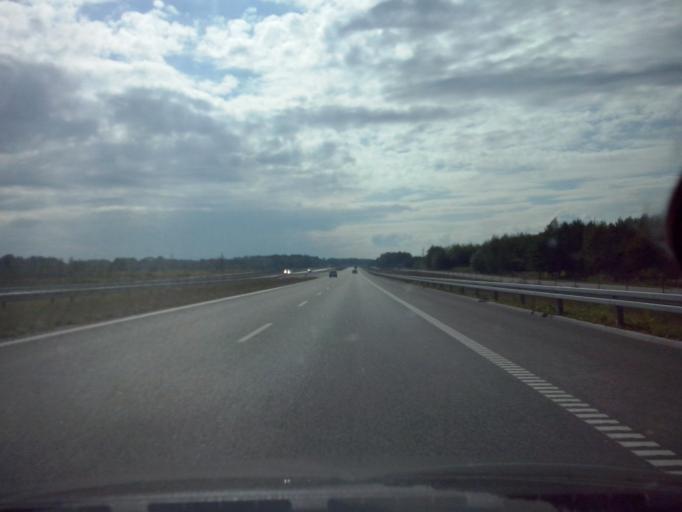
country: PL
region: Lesser Poland Voivodeship
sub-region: Powiat tarnowski
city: Lisia Gora
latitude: 50.0741
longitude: 21.0877
